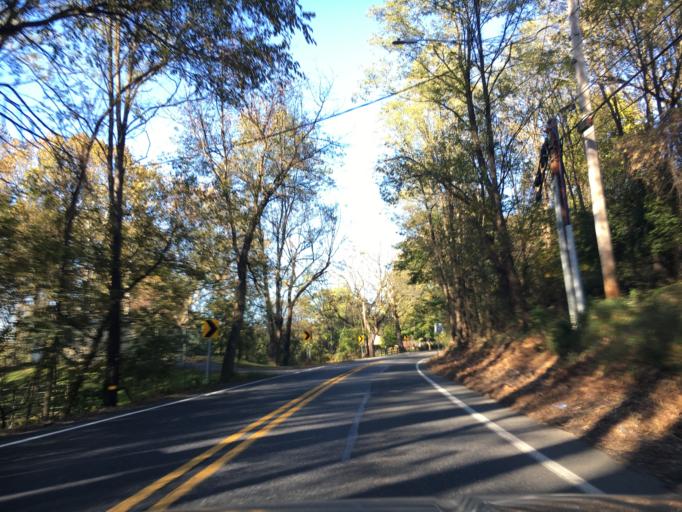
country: US
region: Pennsylvania
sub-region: Lehigh County
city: Fullerton
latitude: 40.6356
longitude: -75.4627
